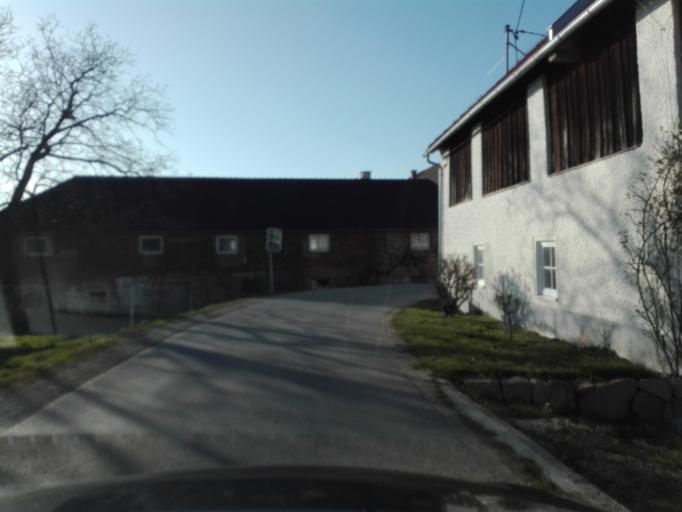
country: AT
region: Upper Austria
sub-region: Politischer Bezirk Perg
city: Bad Kreuzen
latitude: 48.2641
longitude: 14.7374
